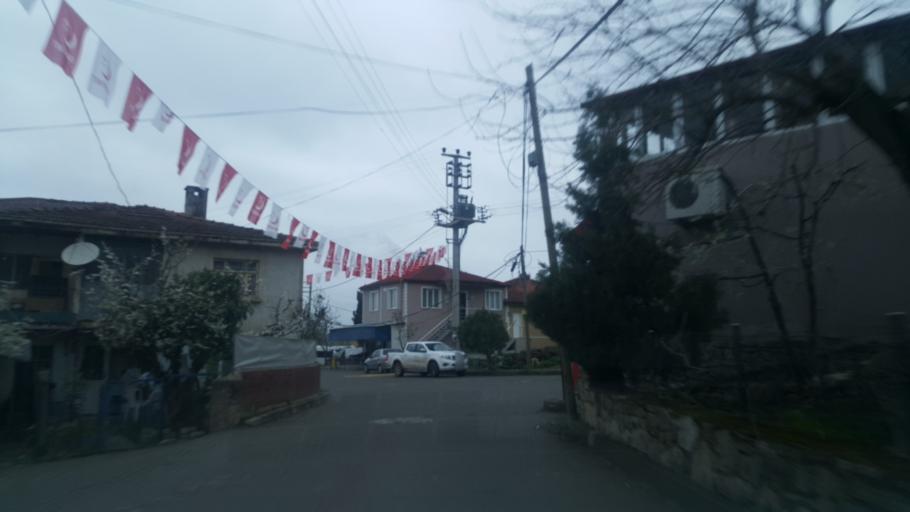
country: TR
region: Kocaeli
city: Tavsanli
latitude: 40.8465
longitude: 29.5550
